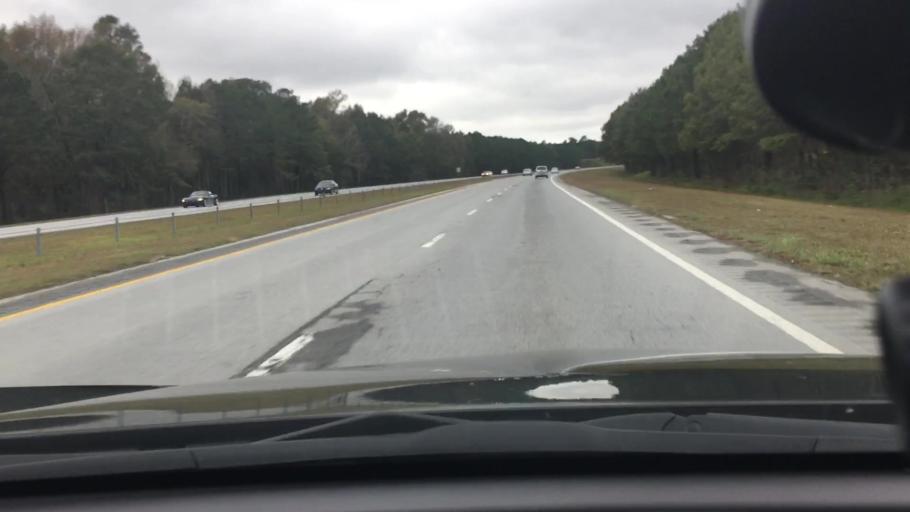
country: US
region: North Carolina
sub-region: Pitt County
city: Farmville
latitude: 35.6210
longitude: -77.6999
